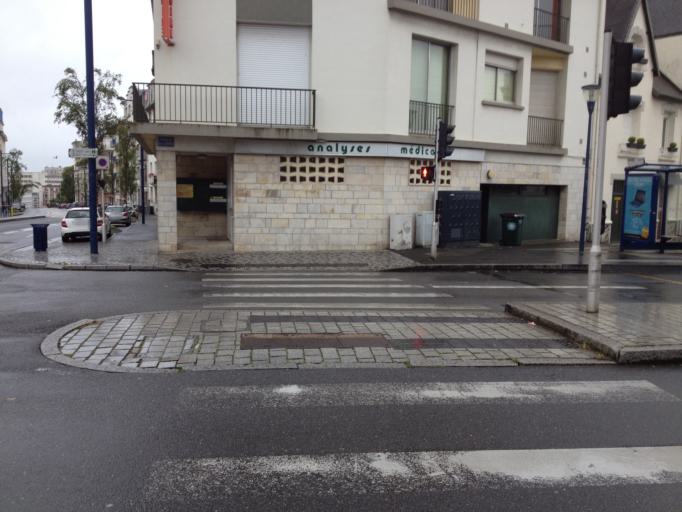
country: FR
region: Brittany
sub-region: Departement du Finistere
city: Brest
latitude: 48.3962
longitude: -4.4840
